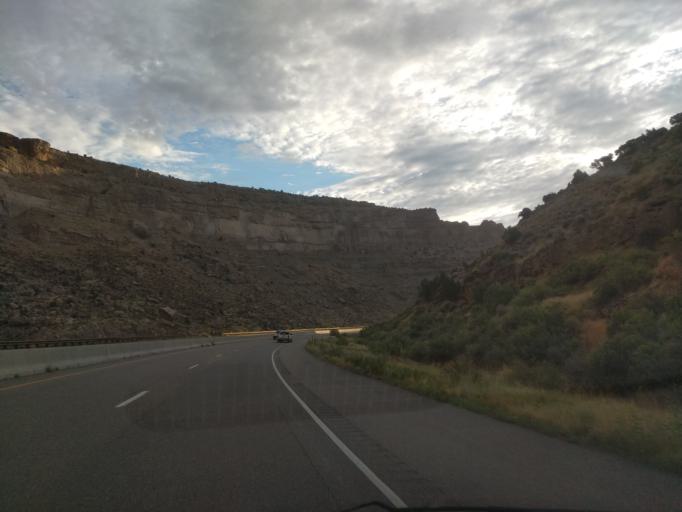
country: US
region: Colorado
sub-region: Mesa County
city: Palisade
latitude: 39.1937
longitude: -108.2811
